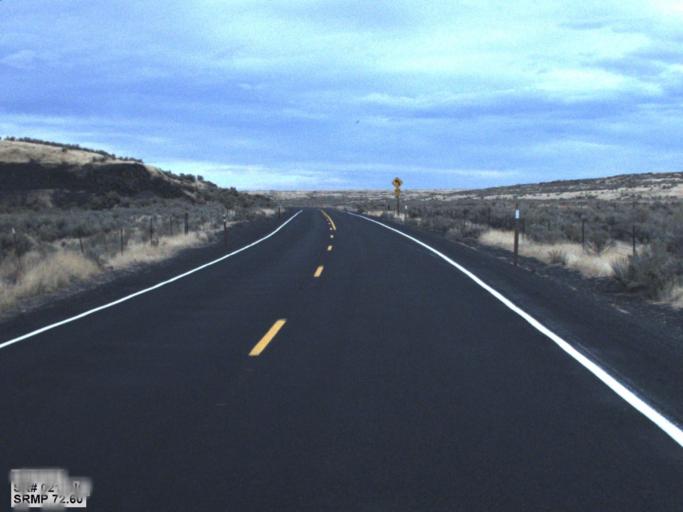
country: US
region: Washington
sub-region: Okanogan County
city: Coulee Dam
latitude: 47.5326
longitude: -118.7820
